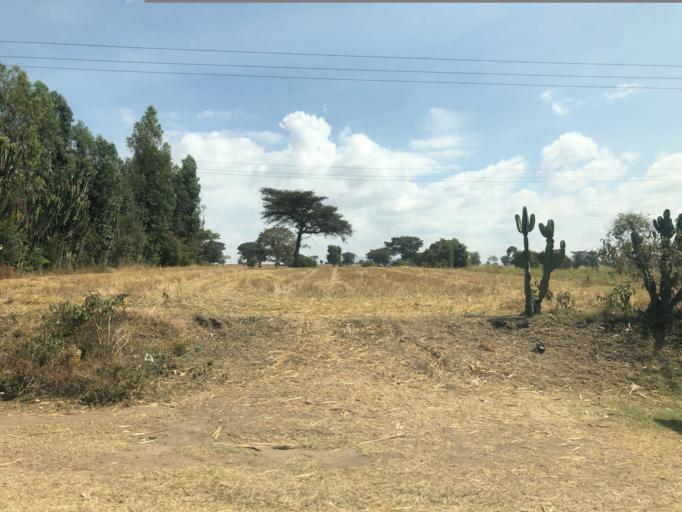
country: ET
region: Oromiya
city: Shashemene
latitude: 7.3204
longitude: 38.6551
